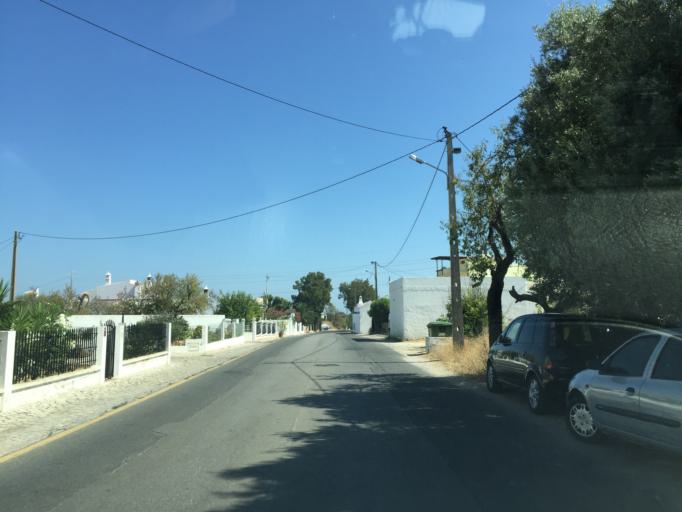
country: PT
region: Faro
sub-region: Olhao
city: Olhao
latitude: 37.0481
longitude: -7.8647
